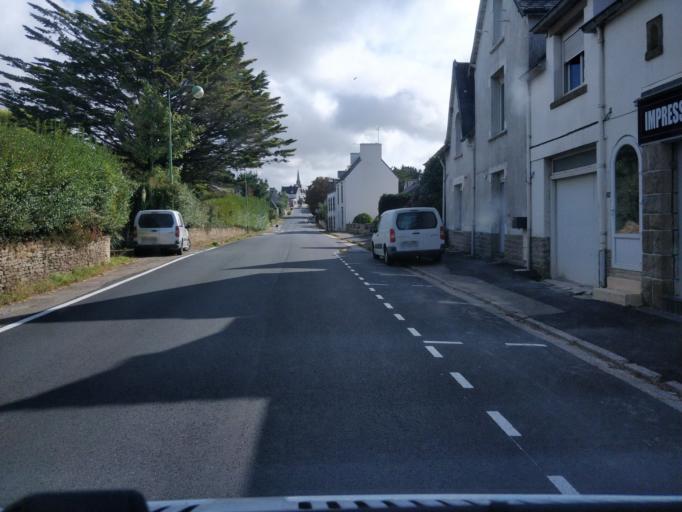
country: FR
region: Brittany
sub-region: Departement du Finistere
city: Landudec
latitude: 48.0002
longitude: -4.3417
